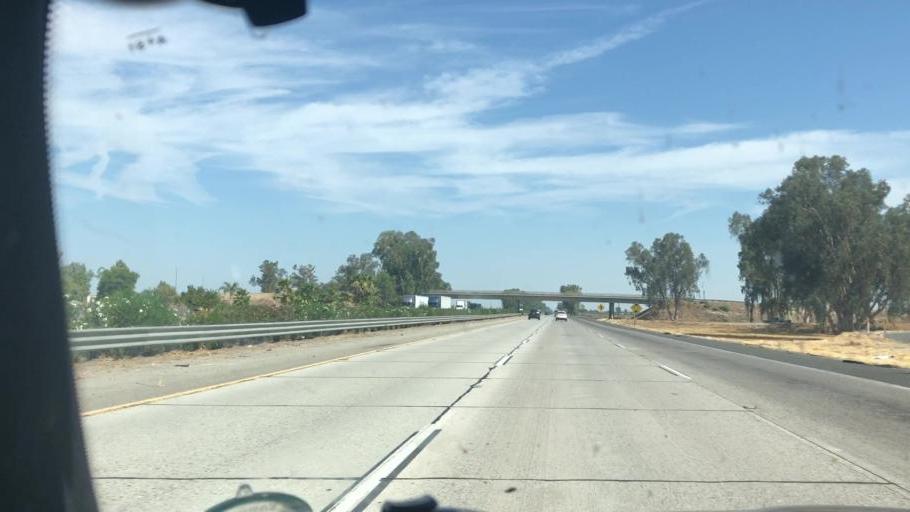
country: US
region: California
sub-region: Kern County
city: Greenfield
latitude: 35.2352
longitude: -119.0146
